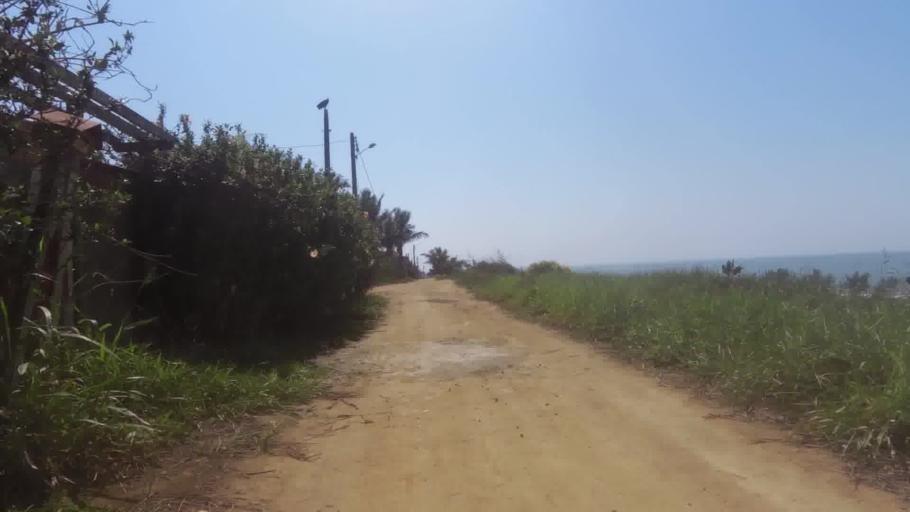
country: BR
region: Espirito Santo
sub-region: Marataizes
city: Marataizes
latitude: -21.1114
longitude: -40.8559
